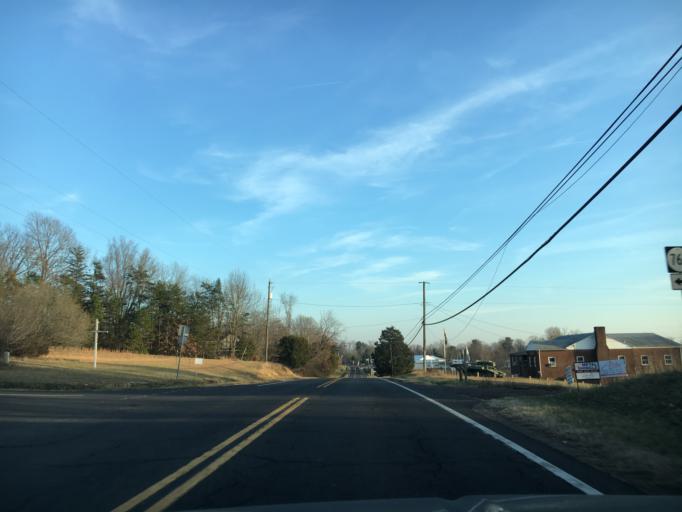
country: US
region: Virginia
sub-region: Culpeper County
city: Culpeper
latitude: 38.4873
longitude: -78.0252
